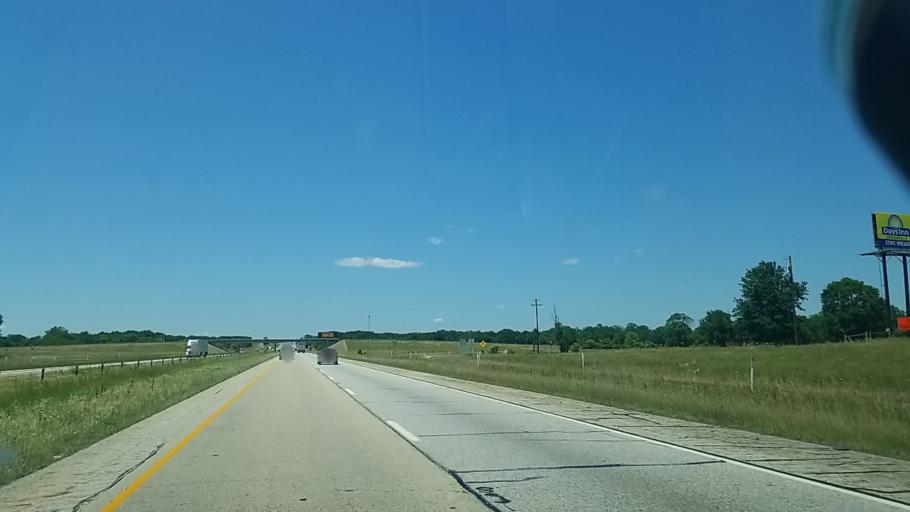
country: US
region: Texas
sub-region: Leon County
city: Centerville
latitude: 31.1462
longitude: -95.9822
